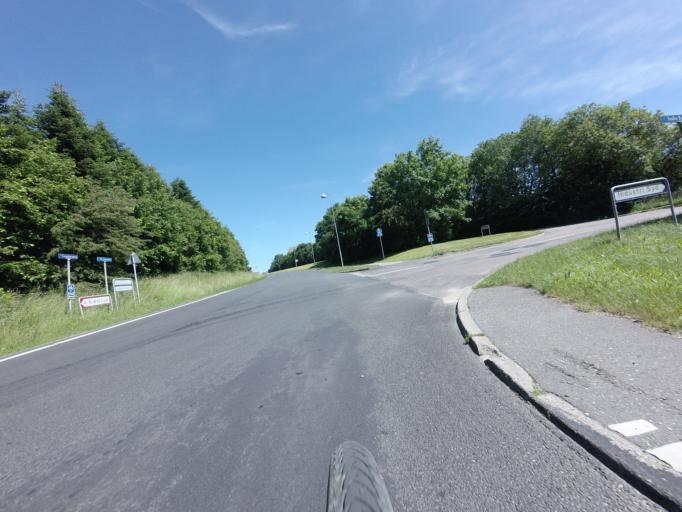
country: DK
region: Central Jutland
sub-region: Horsens Kommune
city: Braedstrup
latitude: 55.9761
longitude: 9.6033
